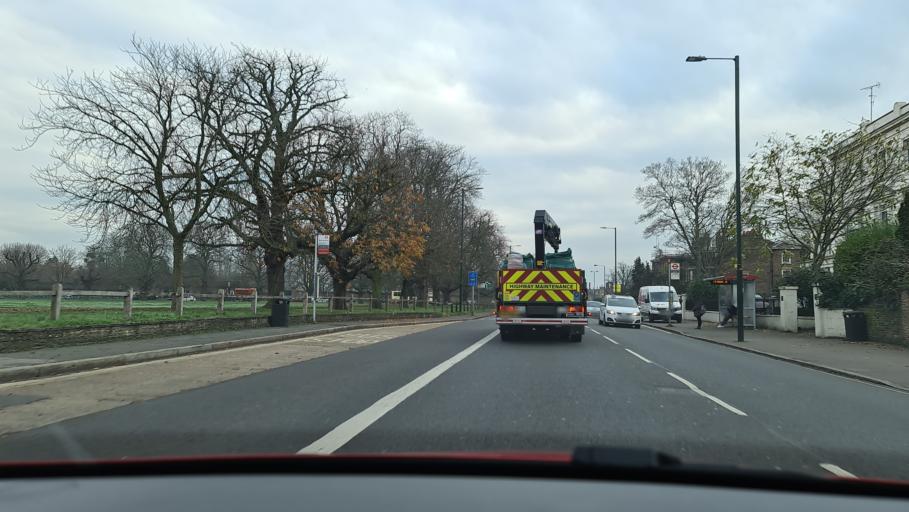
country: GB
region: England
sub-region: Surrey
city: East Molesey
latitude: 51.4061
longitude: -0.3434
